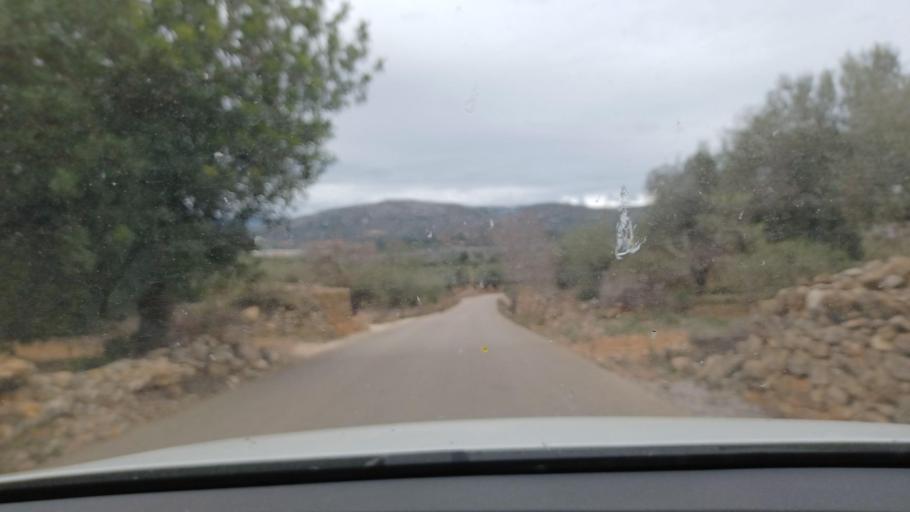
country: ES
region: Valencia
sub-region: Provincia de Castello
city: Traiguera
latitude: 40.5107
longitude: 0.2941
